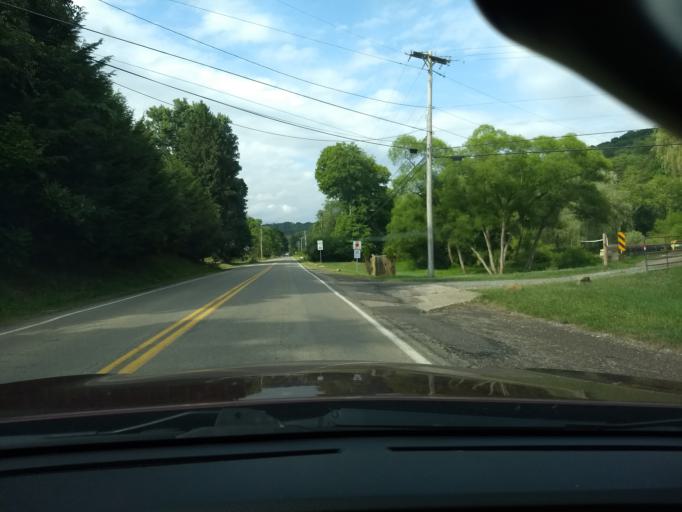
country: US
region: Pennsylvania
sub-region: Allegheny County
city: Bell Acres
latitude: 40.6146
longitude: -80.1434
